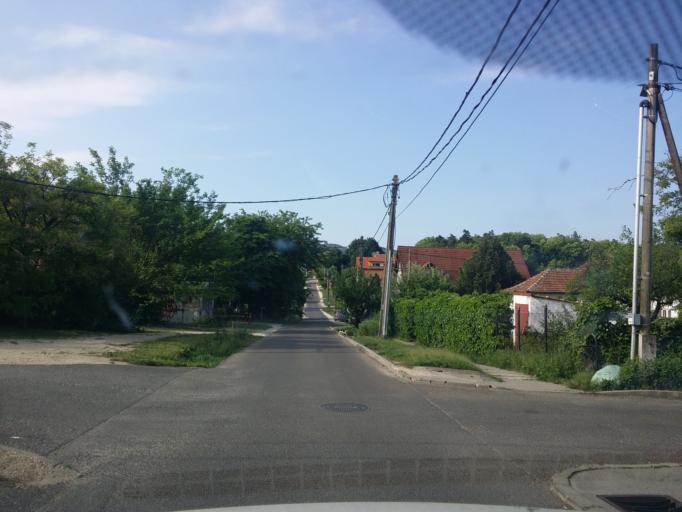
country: HU
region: Pest
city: Urom
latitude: 47.5942
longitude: 19.0155
